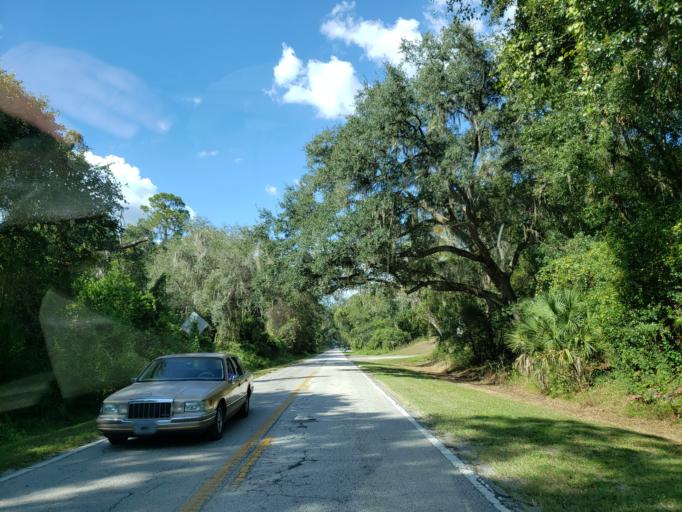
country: US
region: Florida
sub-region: Hillsborough County
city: Valrico
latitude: 27.9392
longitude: -82.2030
